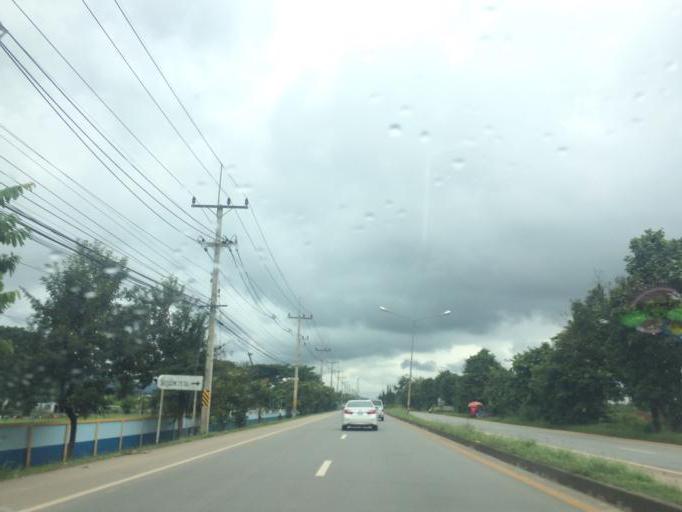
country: TH
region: Chiang Rai
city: Mae Chan
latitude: 20.0324
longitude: 99.8741
